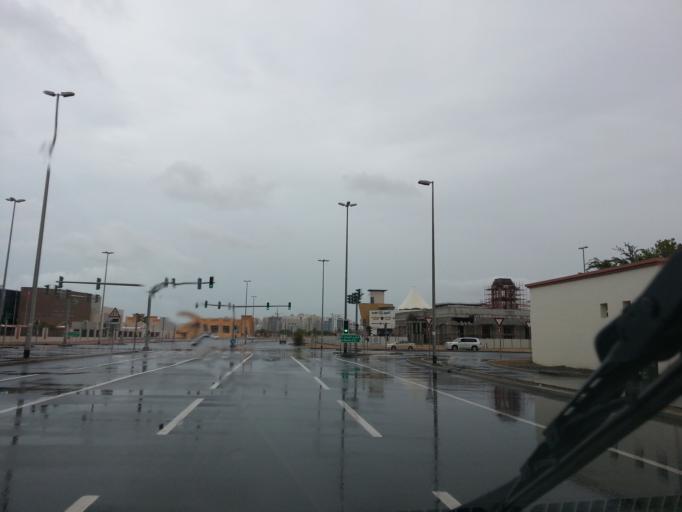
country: AE
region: Dubai
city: Dubai
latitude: 25.0963
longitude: 55.2033
